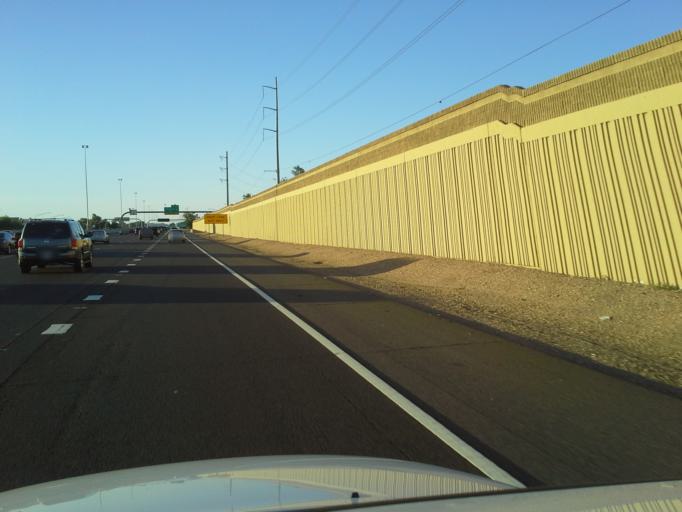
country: US
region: Arizona
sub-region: Maricopa County
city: Glendale
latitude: 33.6045
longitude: -112.1165
